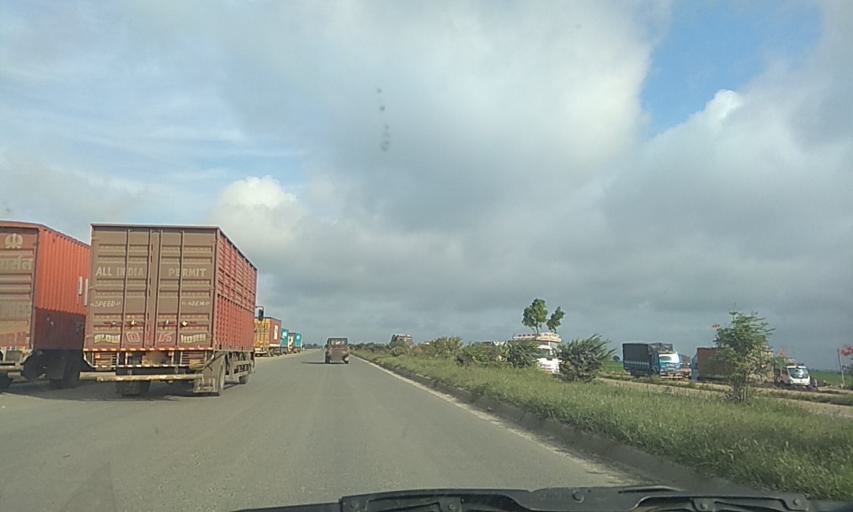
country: IN
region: Karnataka
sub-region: Haveri
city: Savanur
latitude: 14.8875
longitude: 75.3027
